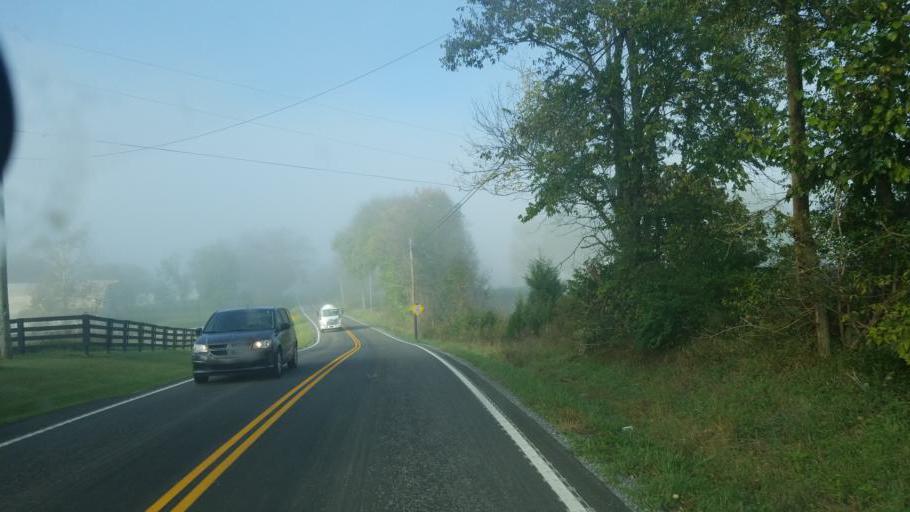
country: US
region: Kentucky
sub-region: Fleming County
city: Flemingsburg
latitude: 38.4882
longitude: -83.6288
